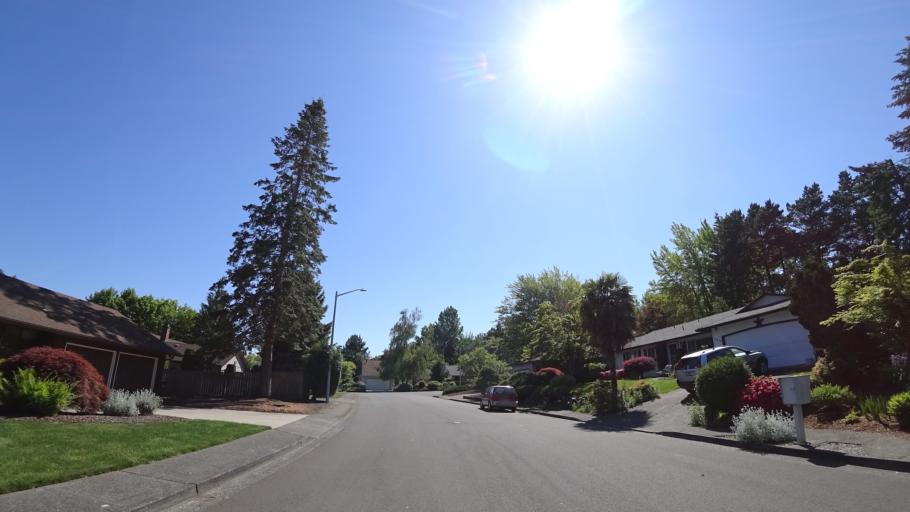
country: US
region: Oregon
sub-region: Washington County
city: Beaverton
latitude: 45.4590
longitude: -122.7998
